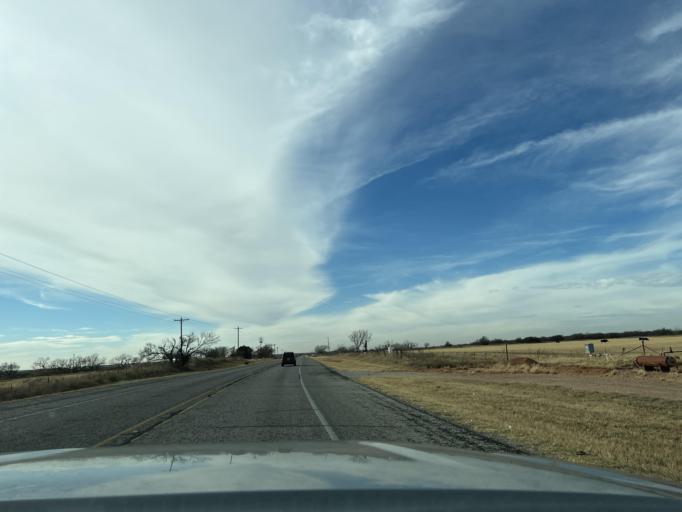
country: US
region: Texas
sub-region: Fisher County
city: Roby
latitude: 32.7541
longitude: -100.2633
